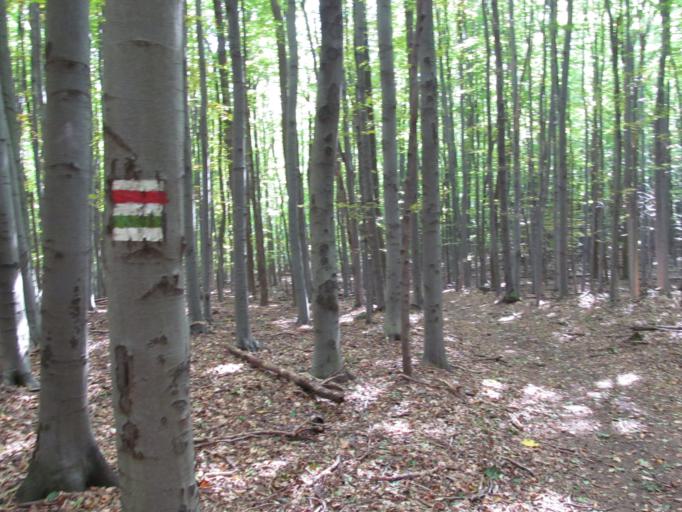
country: HU
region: Nograd
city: Diosjeno
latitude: 47.9559
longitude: 18.9417
